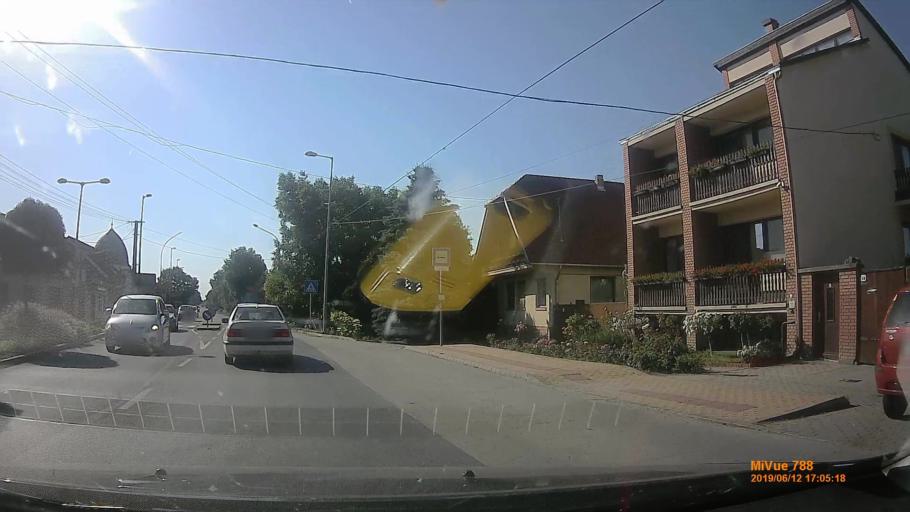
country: HU
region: Csongrad
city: Deszk
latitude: 46.2222
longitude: 20.1961
